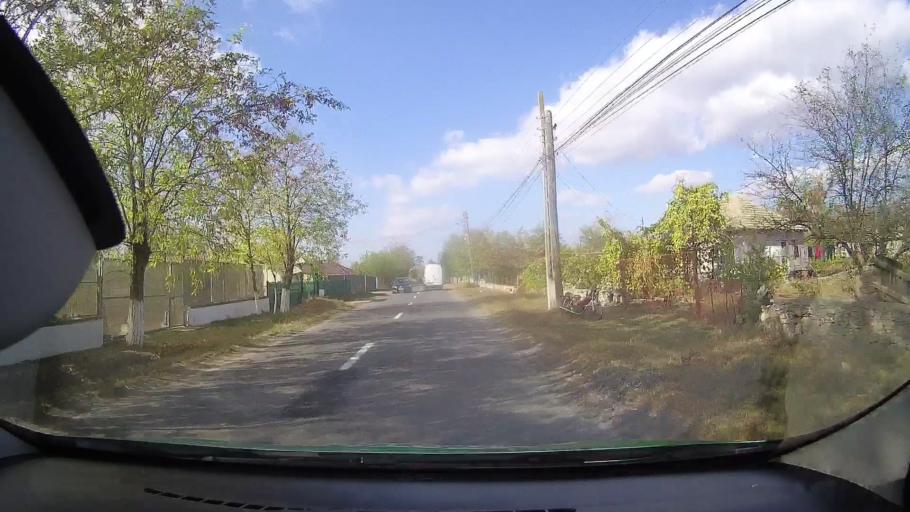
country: RO
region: Constanta
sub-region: Comuna Istria
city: Nuntasi
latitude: 44.5394
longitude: 28.6501
